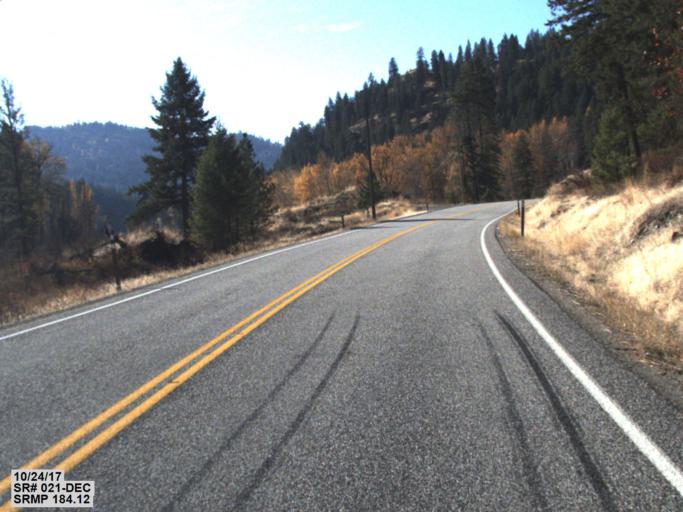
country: CA
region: British Columbia
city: Grand Forks
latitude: 48.9161
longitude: -118.5666
